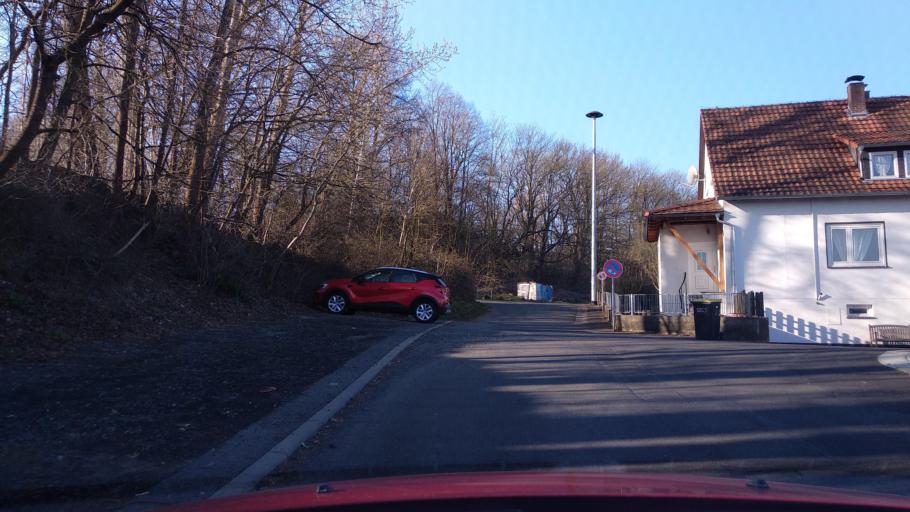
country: DE
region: Hesse
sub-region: Regierungsbezirk Kassel
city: Calden
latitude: 51.3588
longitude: 9.3858
